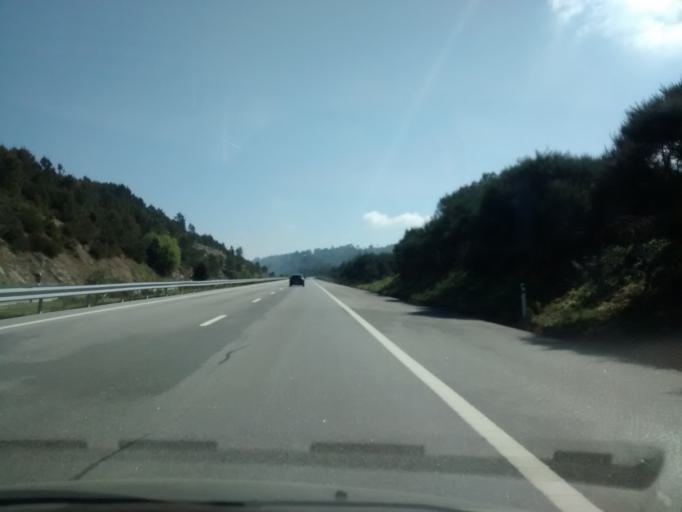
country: PT
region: Braga
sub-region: Cabeceiras de Basto
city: Refojos de Basto
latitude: 41.4640
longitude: -8.0153
